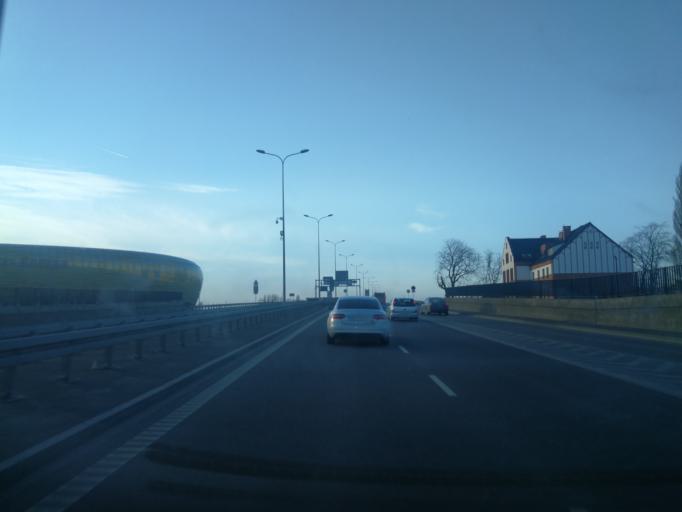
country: PL
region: Pomeranian Voivodeship
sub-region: Gdansk
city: Gdansk
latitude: 54.3896
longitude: 18.6473
